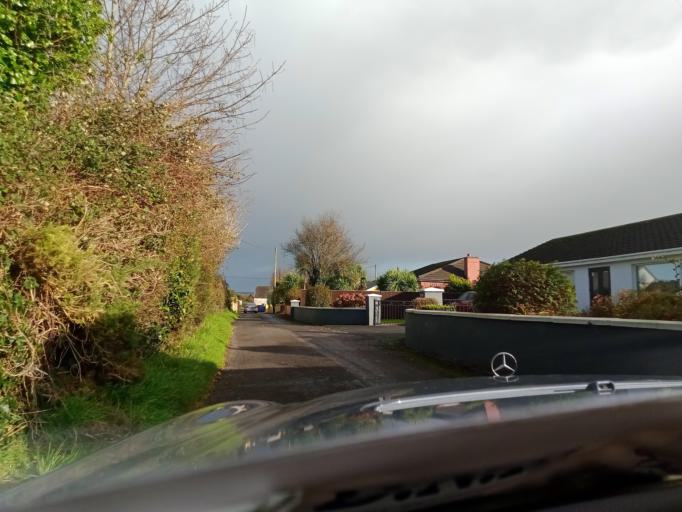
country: IE
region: Leinster
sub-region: Kilkenny
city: Mooncoin
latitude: 52.2998
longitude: -7.2720
